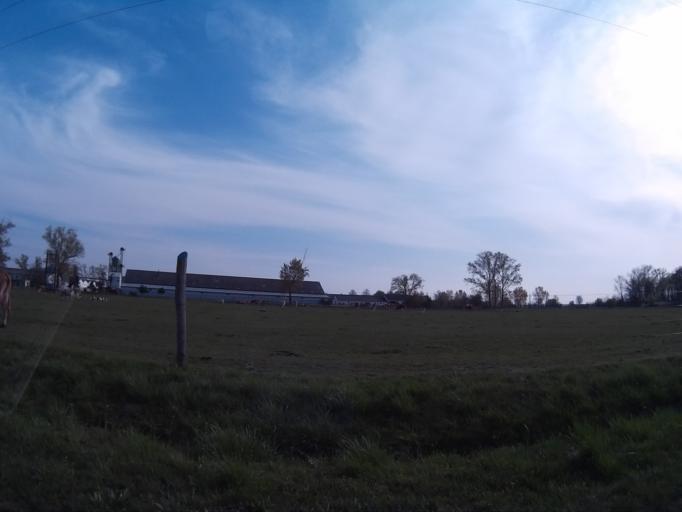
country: HU
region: Vas
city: Celldomolk
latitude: 47.1880
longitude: 17.0930
